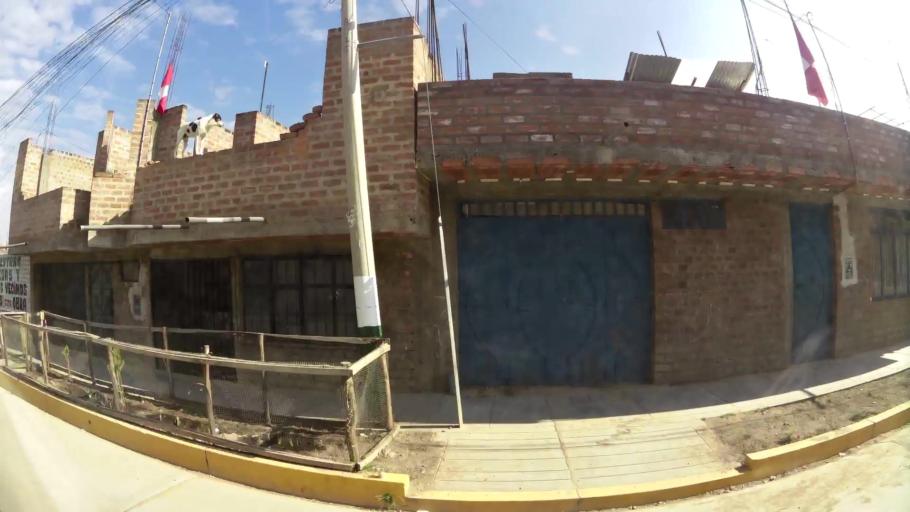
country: PE
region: Junin
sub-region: Provincia de Huancayo
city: Huancayo
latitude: -12.0570
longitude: -75.1958
